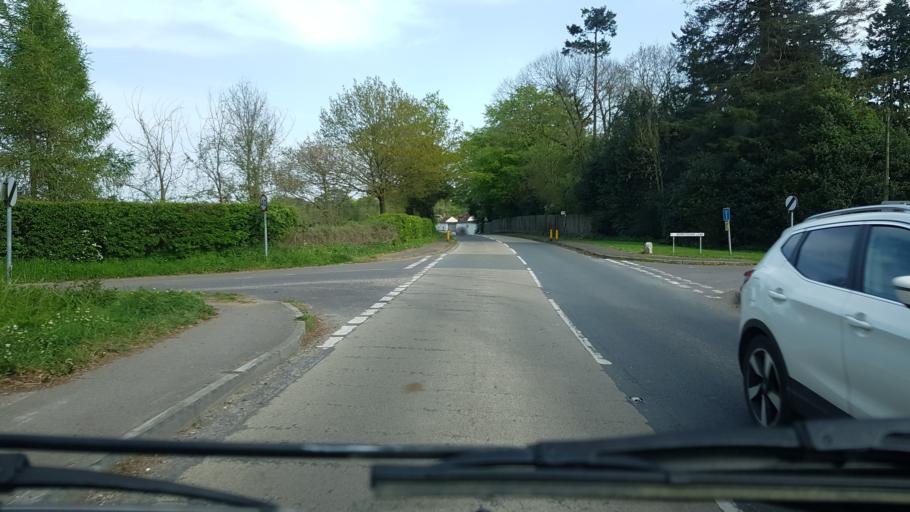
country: GB
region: England
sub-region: Hampshire
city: Overton
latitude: 51.2436
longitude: -1.2506
